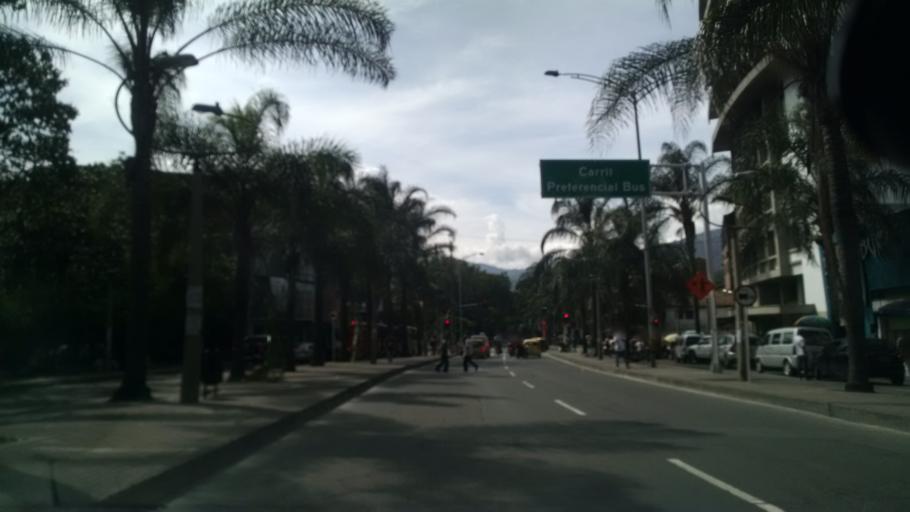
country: CO
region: Antioquia
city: Medellin
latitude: 6.2531
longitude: -75.5696
